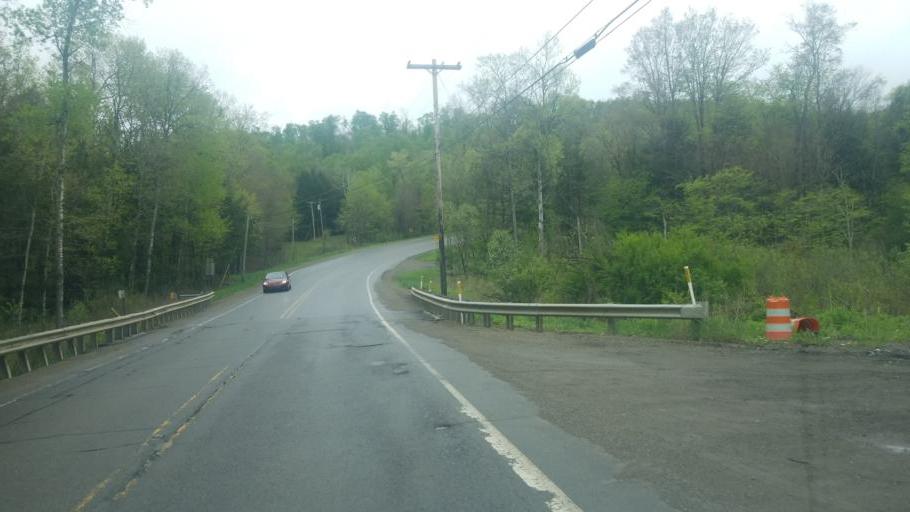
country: US
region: Pennsylvania
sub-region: McKean County
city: Kane
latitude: 41.6276
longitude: -78.8252
